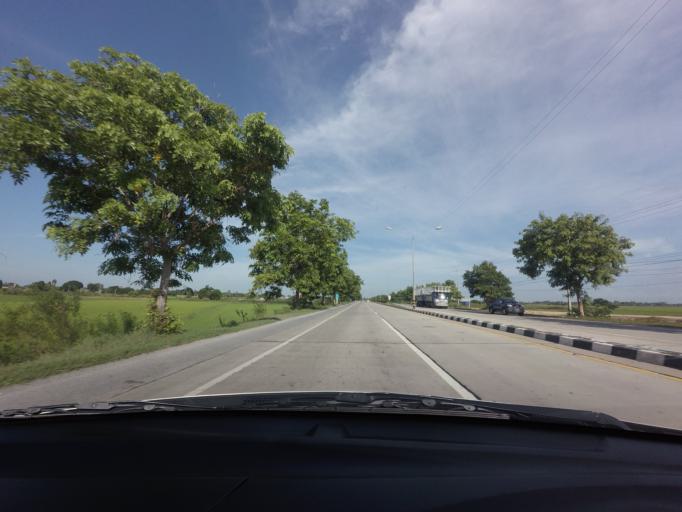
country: TH
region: Suphan Buri
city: Suphan Buri
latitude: 14.4606
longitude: 100.0527
